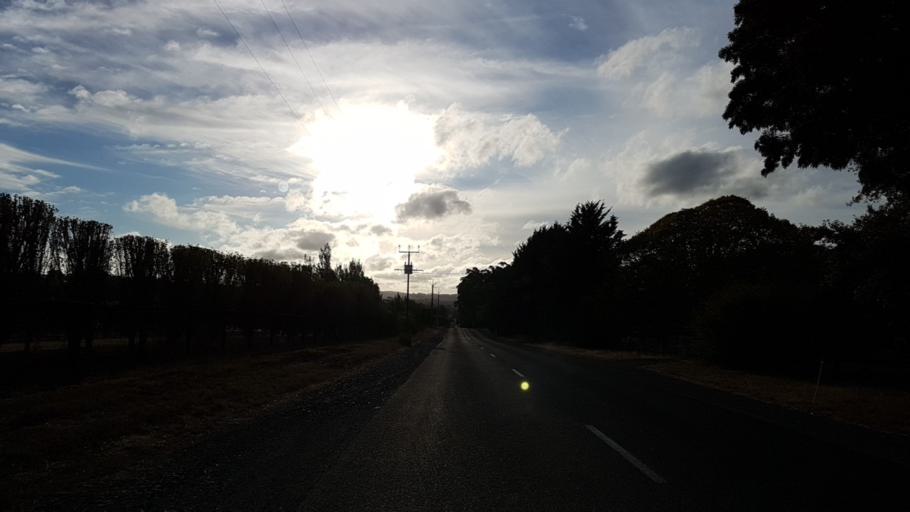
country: AU
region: South Australia
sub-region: Adelaide Hills
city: Woodside
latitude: -34.9778
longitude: 138.8769
